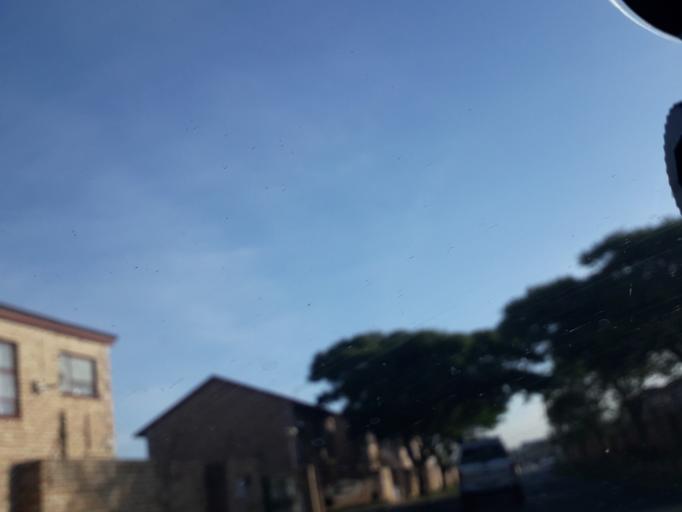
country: ZA
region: Gauteng
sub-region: City of Johannesburg Metropolitan Municipality
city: Roodepoort
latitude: -26.1039
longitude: 27.8959
